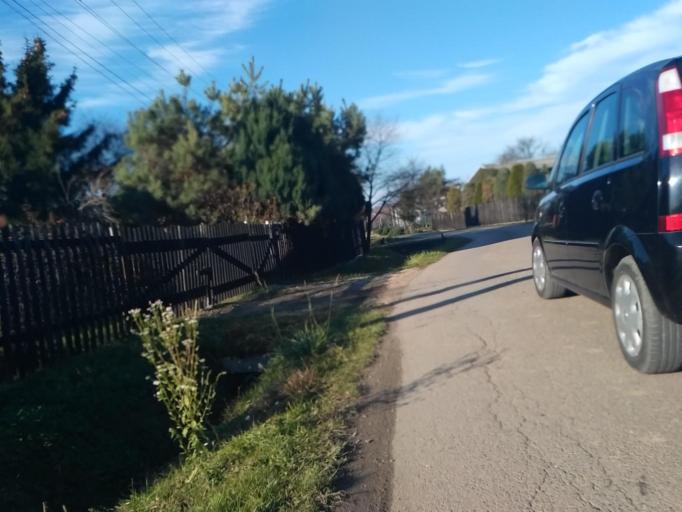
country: PL
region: Subcarpathian Voivodeship
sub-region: Powiat brzozowski
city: Humniska
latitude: 49.6732
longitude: 22.0494
